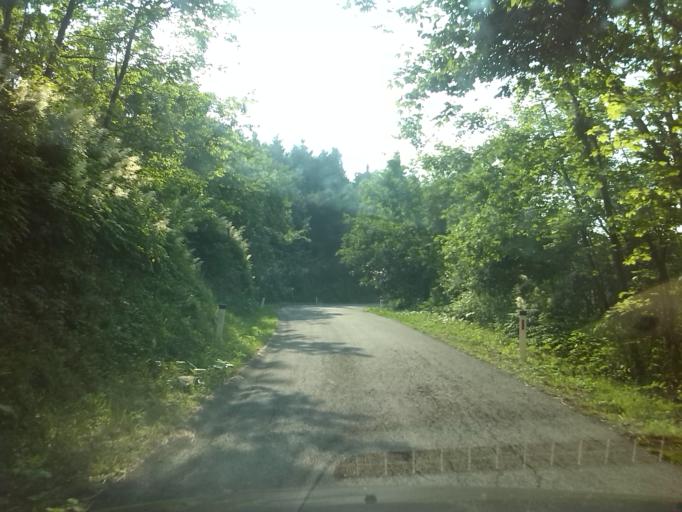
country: IT
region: Friuli Venezia Giulia
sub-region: Provincia di Udine
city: Cras
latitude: 46.1868
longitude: 13.6548
